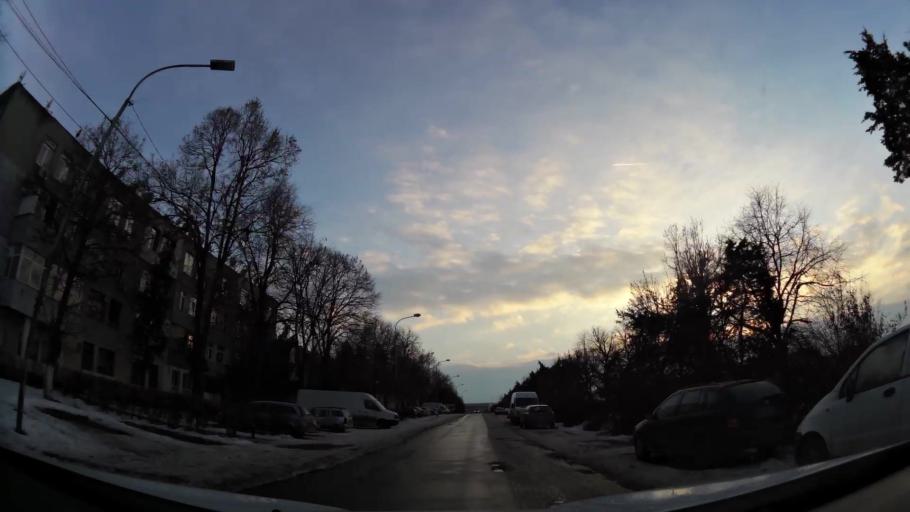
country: RO
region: Ilfov
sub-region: Comuna Popesti-Leordeni
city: Popesti-Leordeni
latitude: 44.3661
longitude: 26.1950
